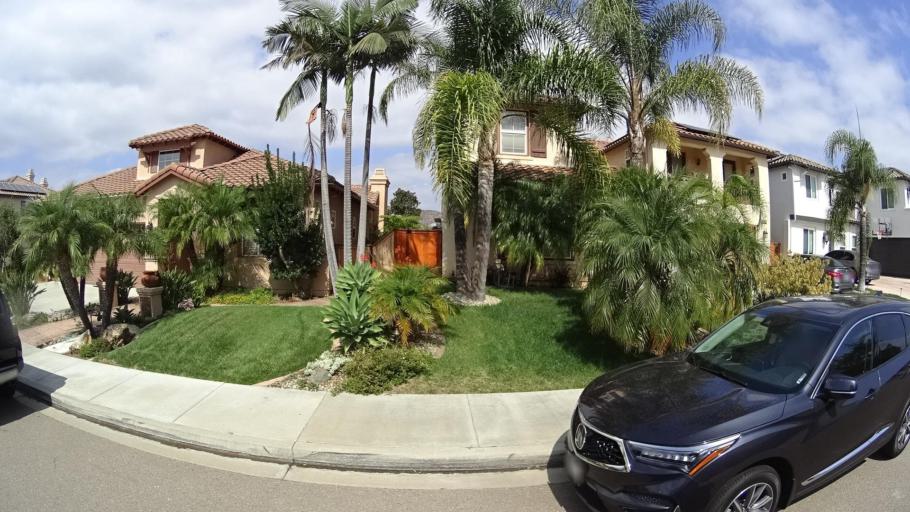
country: US
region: California
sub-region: San Diego County
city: Fairbanks Ranch
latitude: 33.0129
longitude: -117.1070
